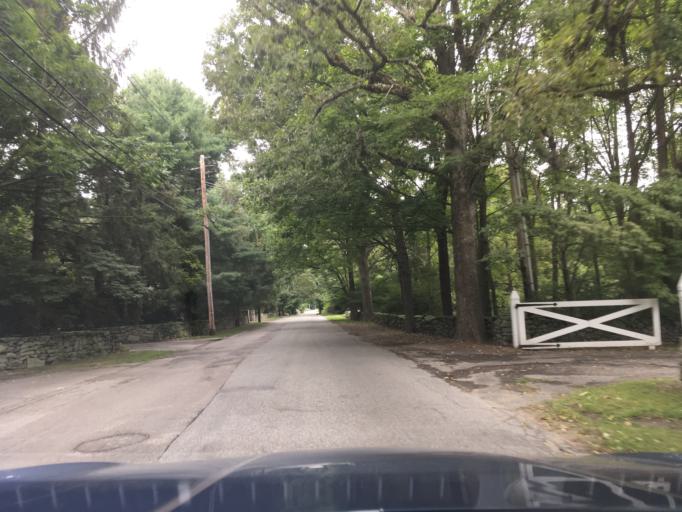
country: US
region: Rhode Island
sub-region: Bristol County
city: Barrington
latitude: 41.7190
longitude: -71.3029
